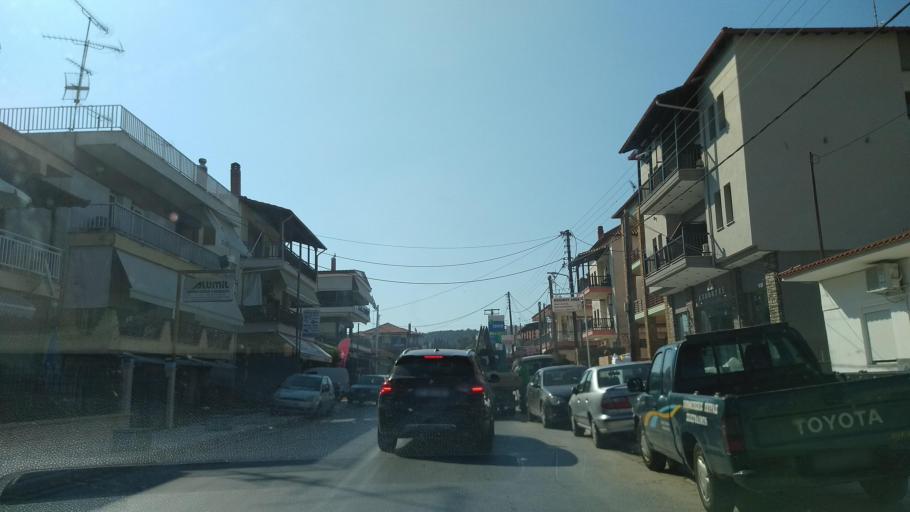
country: GR
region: Central Macedonia
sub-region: Nomos Chalkidikis
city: Ierissos
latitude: 40.3989
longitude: 23.8729
